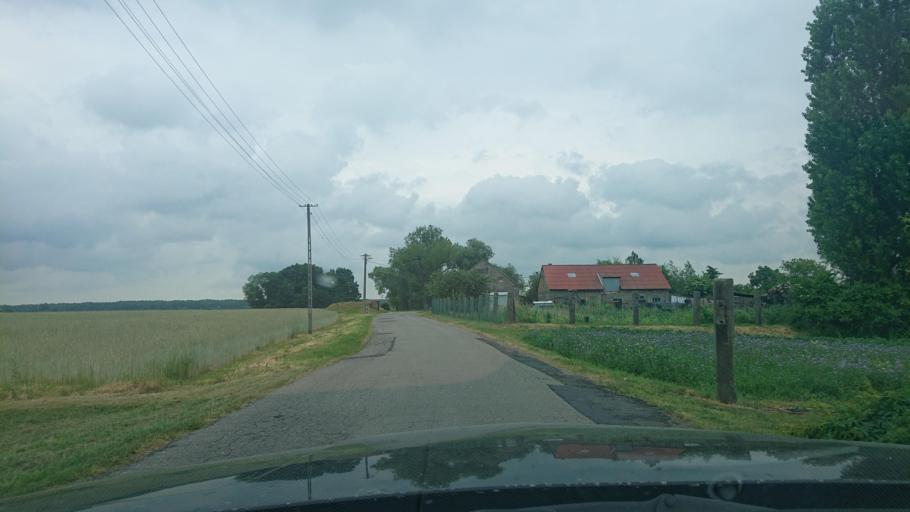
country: PL
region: Greater Poland Voivodeship
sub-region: Powiat gnieznienski
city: Gniezno
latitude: 52.4797
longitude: 17.5495
